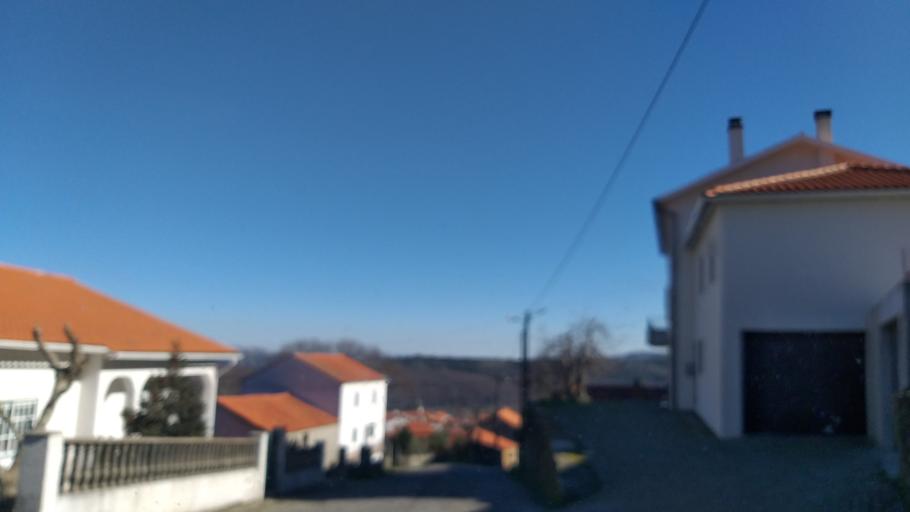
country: PT
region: Guarda
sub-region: Celorico da Beira
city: Celorico da Beira
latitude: 40.5170
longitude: -7.3972
